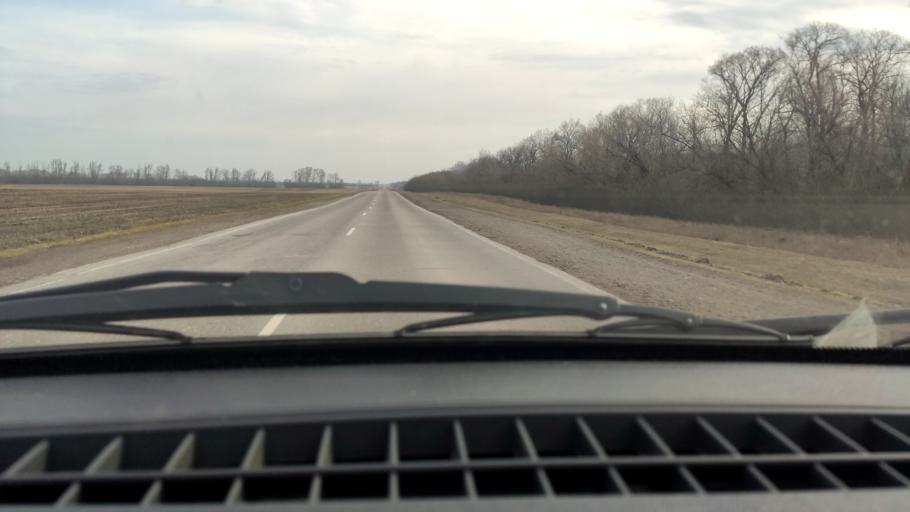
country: RU
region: Bashkortostan
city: Davlekanovo
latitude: 54.2503
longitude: 55.0802
